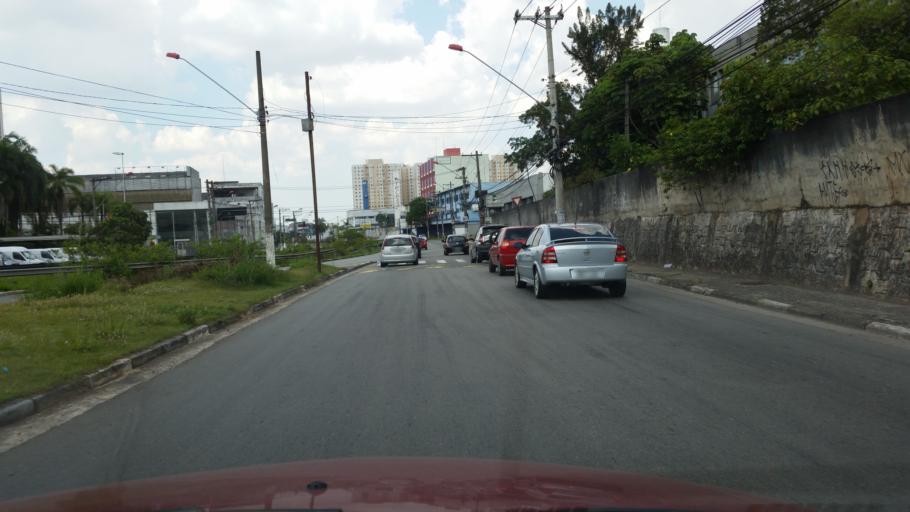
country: BR
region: Sao Paulo
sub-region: Diadema
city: Diadema
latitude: -23.6845
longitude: -46.6044
